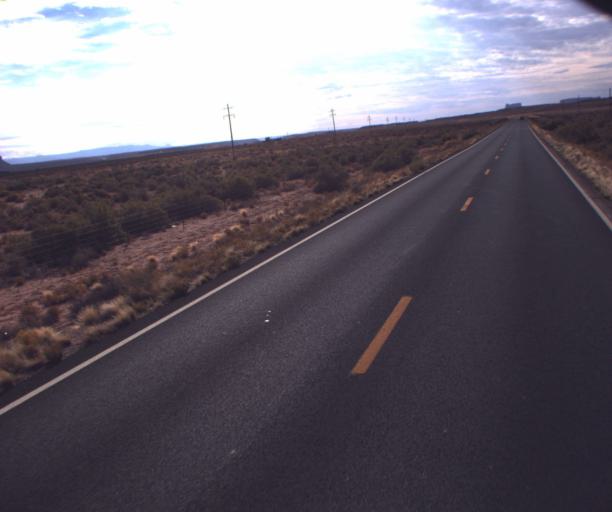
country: US
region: Arizona
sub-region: Apache County
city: Many Farms
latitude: 36.6241
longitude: -109.5828
